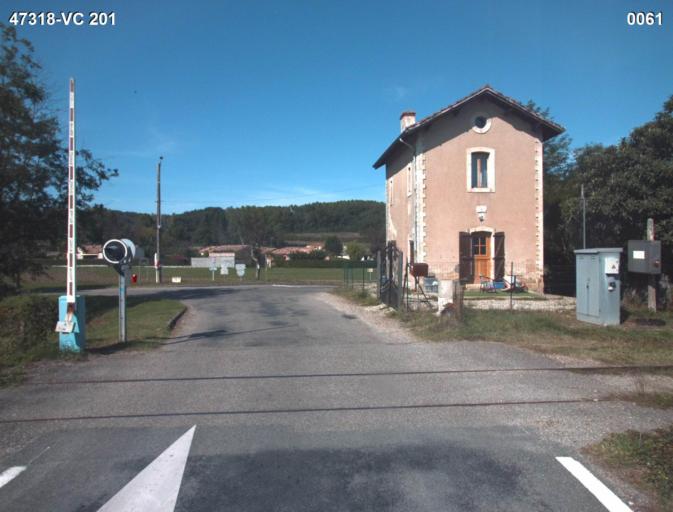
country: FR
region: Aquitaine
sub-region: Departement du Lot-et-Garonne
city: Vianne
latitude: 44.1995
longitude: 0.3230
